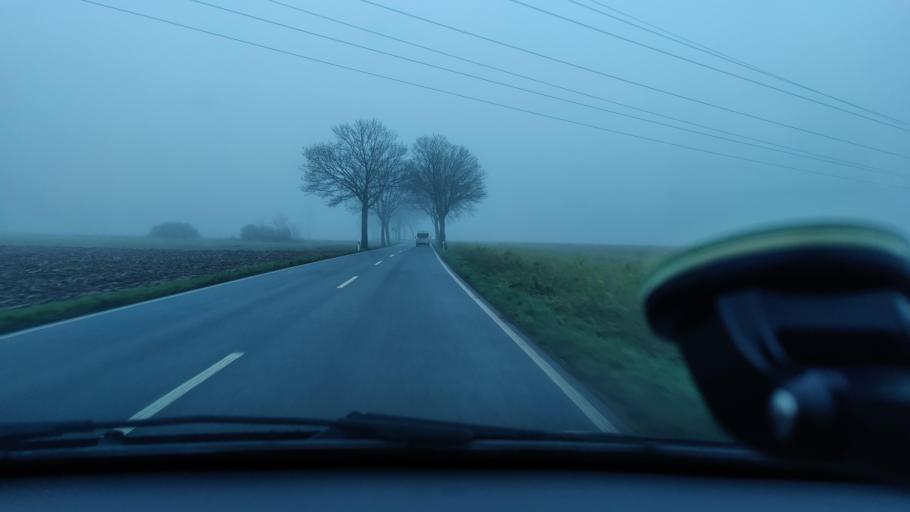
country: DE
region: North Rhine-Westphalia
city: Rees
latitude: 51.7422
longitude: 6.4452
